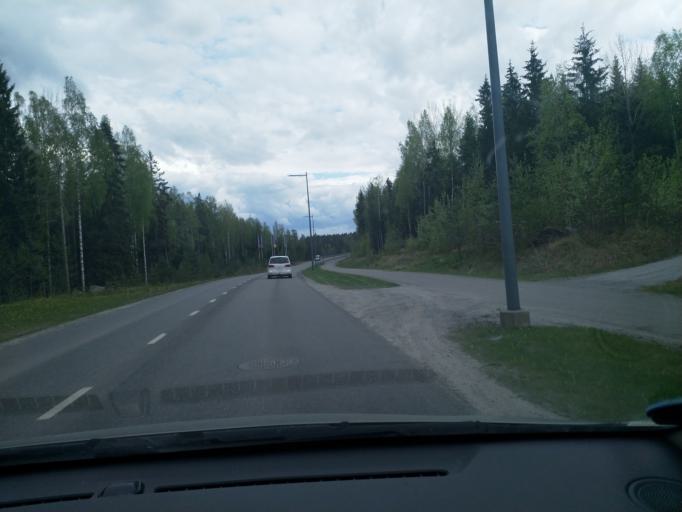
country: FI
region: Pirkanmaa
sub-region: Tampere
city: Tampere
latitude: 61.4523
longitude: 23.8010
